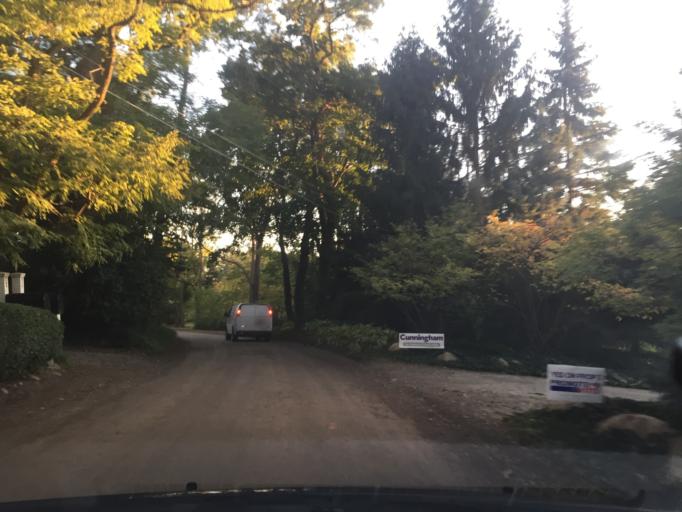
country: US
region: Michigan
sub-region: Oakland County
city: Franklin
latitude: 42.5506
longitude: -83.2938
